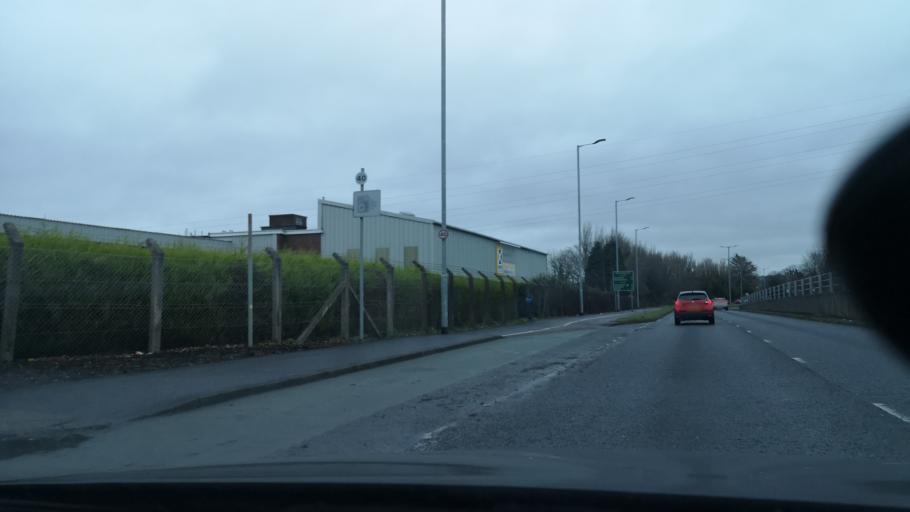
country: GB
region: Northern Ireland
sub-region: Castlereagh District
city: Castlereagh
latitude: 54.5786
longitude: -5.8728
